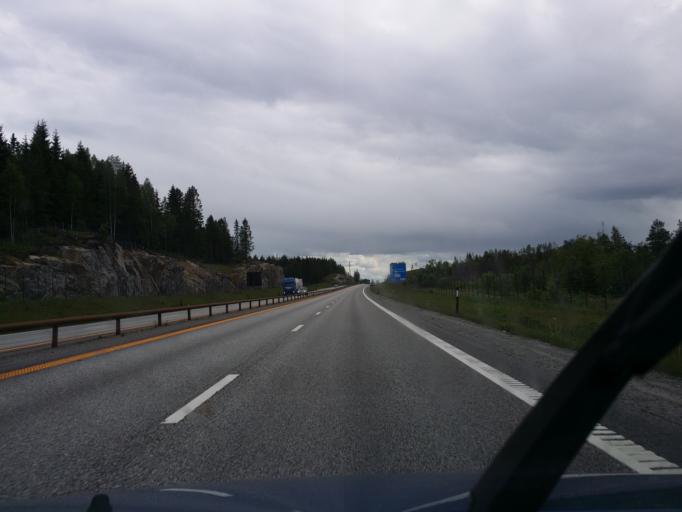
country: NO
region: Akershus
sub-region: Eidsvoll
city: Raholt
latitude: 60.2630
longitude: 11.1719
